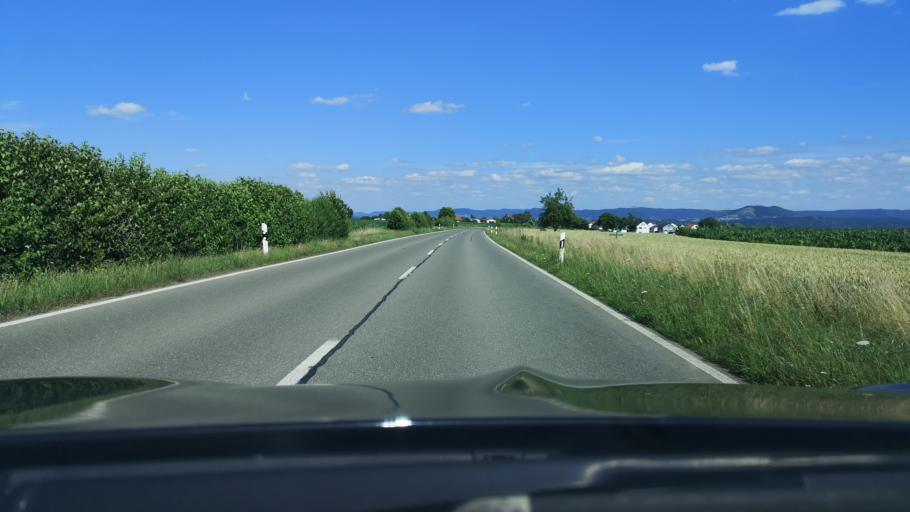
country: DE
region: Baden-Wuerttemberg
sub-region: Regierungsbezirk Stuttgart
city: Altenriet
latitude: 48.5919
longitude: 9.2038
